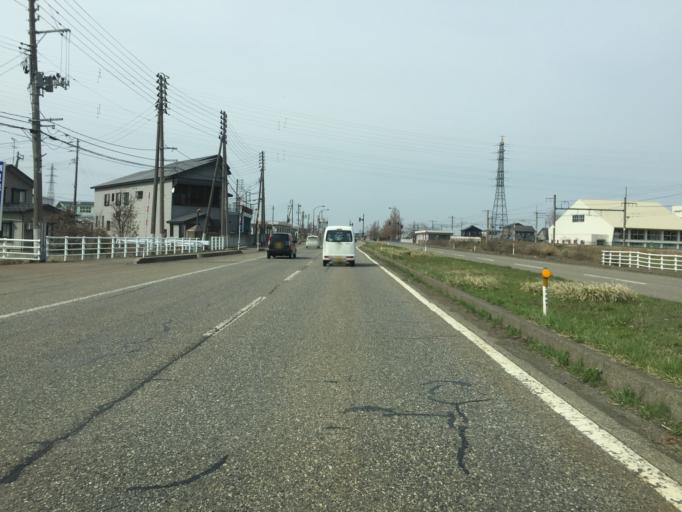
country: JP
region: Niigata
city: Nagaoka
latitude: 37.3729
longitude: 138.8345
